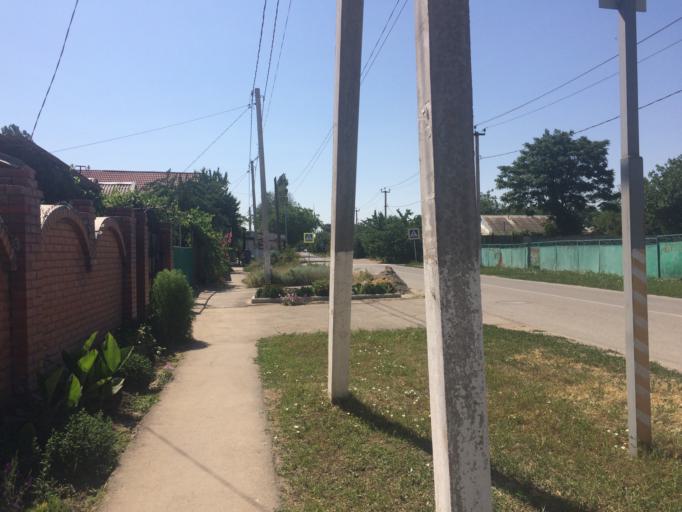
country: RU
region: Rostov
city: Sal'sk
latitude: 46.4760
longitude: 41.5466
